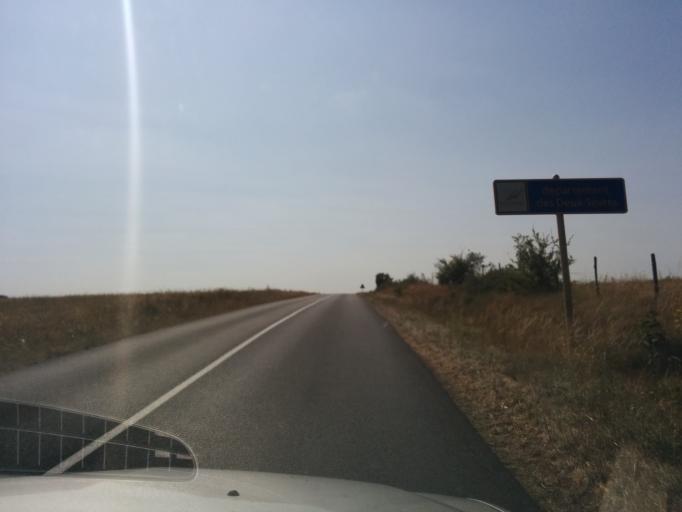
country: FR
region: Poitou-Charentes
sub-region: Departement de la Vienne
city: Moncontour
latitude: 46.8081
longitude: 0.0045
